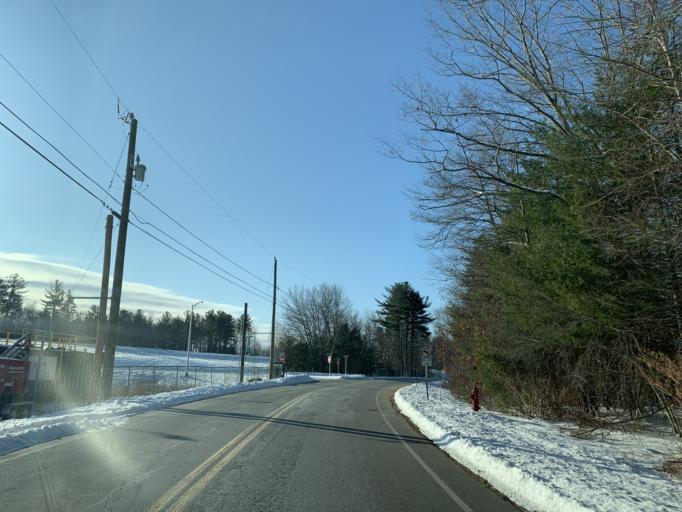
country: US
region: Maine
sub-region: York County
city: Eliot
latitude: 43.1315
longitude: -70.8401
